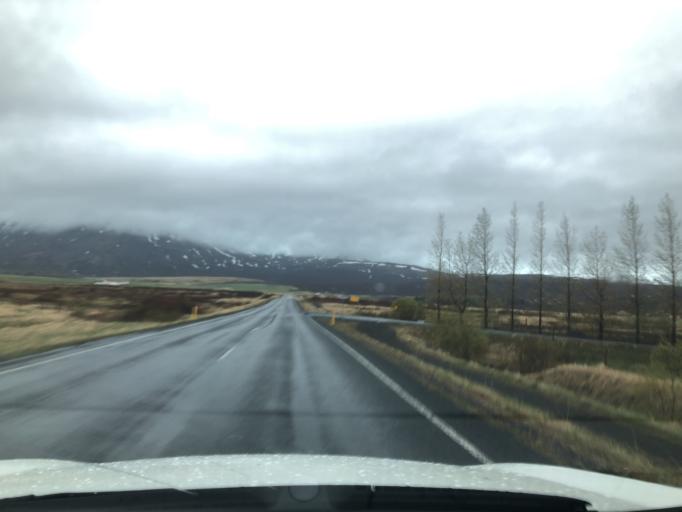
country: IS
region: South
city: Selfoss
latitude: 64.2365
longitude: -20.6459
